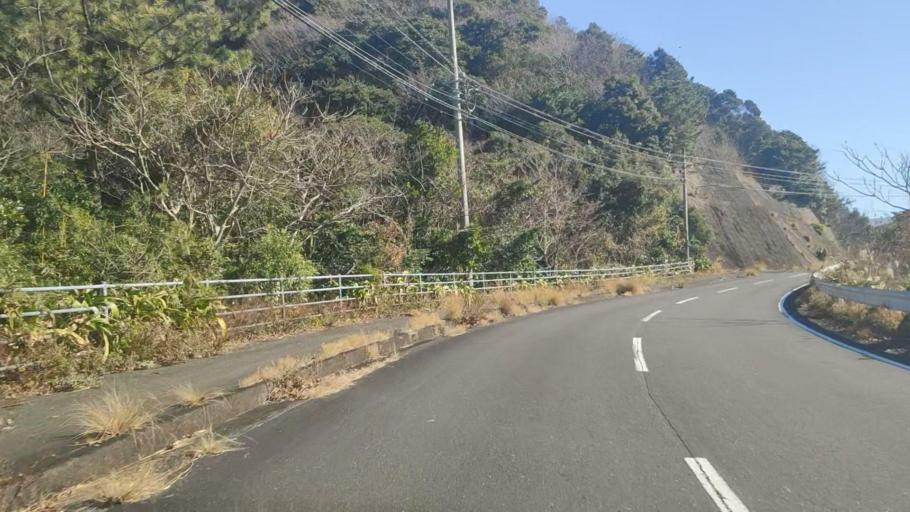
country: JP
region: Oita
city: Saiki
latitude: 32.7951
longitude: 131.8998
